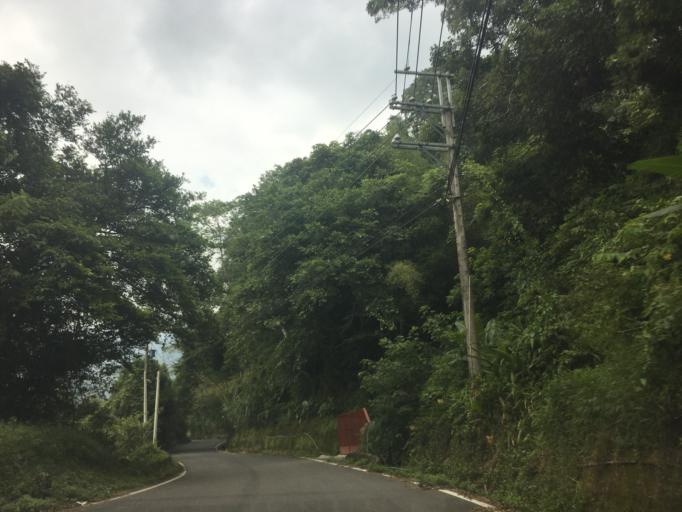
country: TW
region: Taiwan
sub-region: Miaoli
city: Miaoli
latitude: 24.3494
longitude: 120.9452
